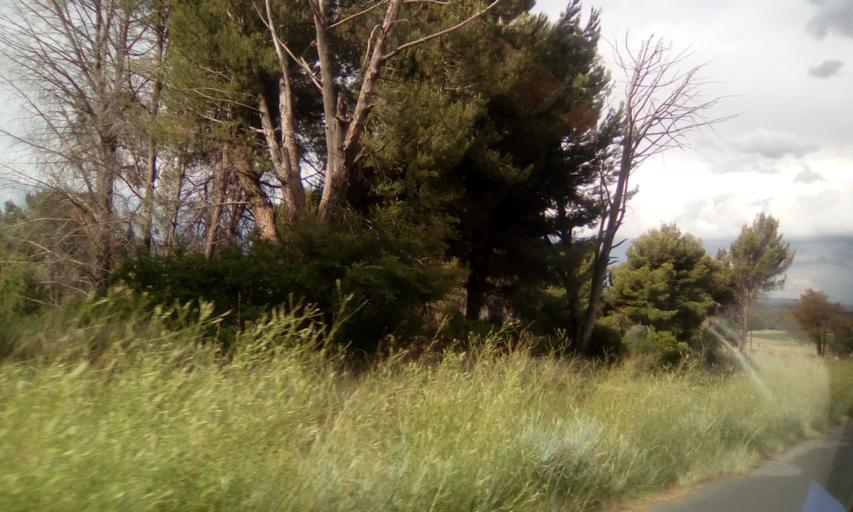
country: ZA
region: Orange Free State
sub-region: Thabo Mofutsanyana District Municipality
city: Ladybrand
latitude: -29.2121
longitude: 27.4639
